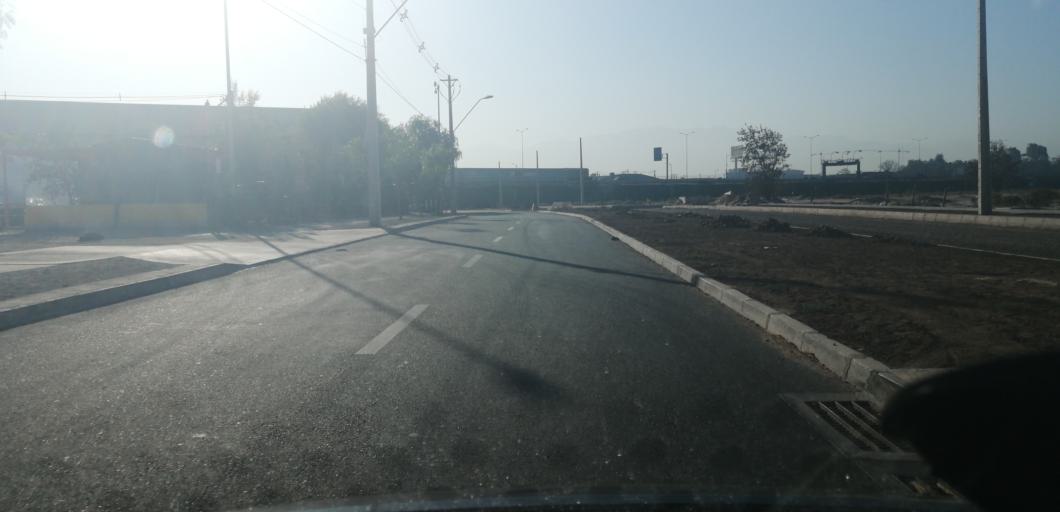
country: CL
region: Santiago Metropolitan
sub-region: Provincia de Santiago
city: Lo Prado
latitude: -33.4377
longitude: -70.7864
